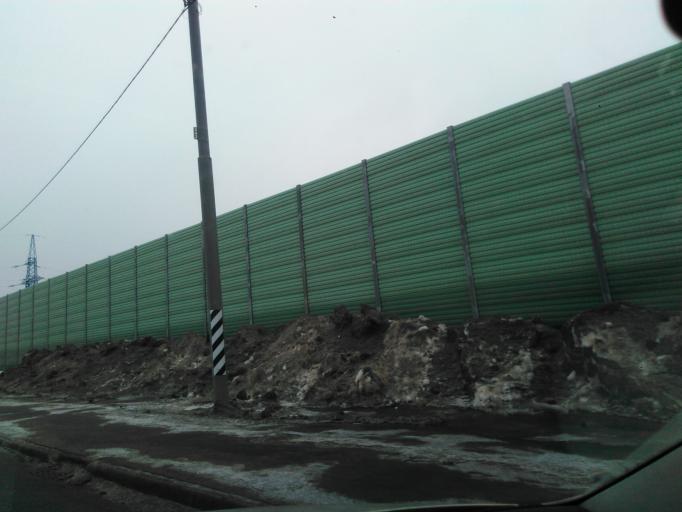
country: RU
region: Moskovskaya
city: Yermolino
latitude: 56.1420
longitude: 37.4934
